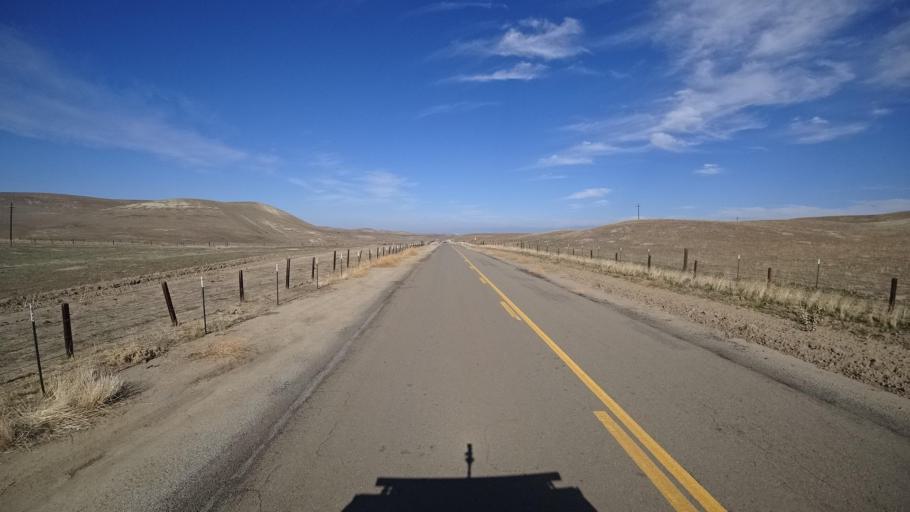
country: US
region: California
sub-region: Tulare County
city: Richgrove
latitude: 35.6368
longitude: -118.9439
